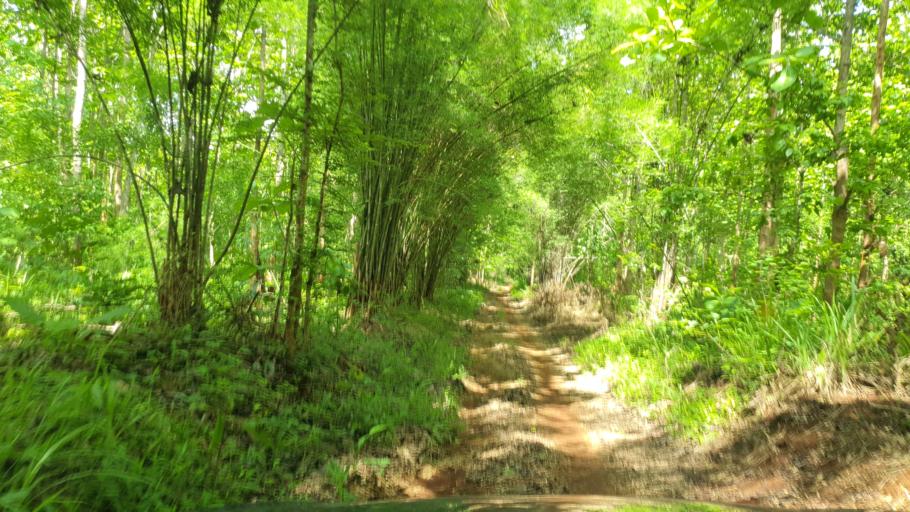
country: TH
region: Chiang Mai
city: Mae Taeng
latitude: 19.0795
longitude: 99.0911
